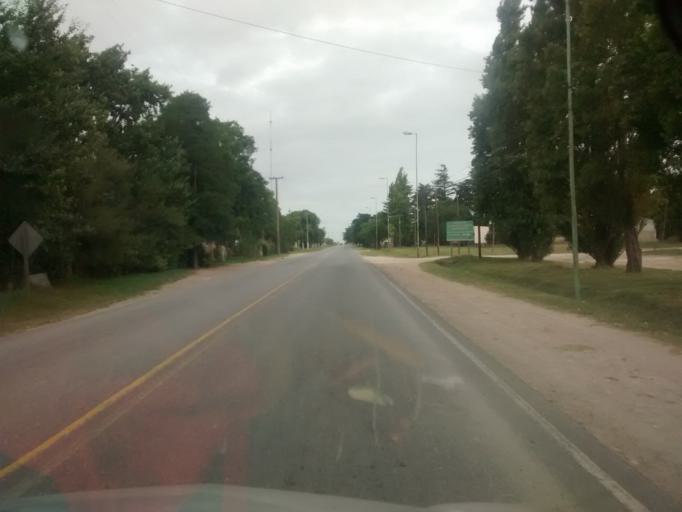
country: AR
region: Buenos Aires
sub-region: Partido de Loberia
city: Loberia
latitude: -38.2000
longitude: -58.7372
